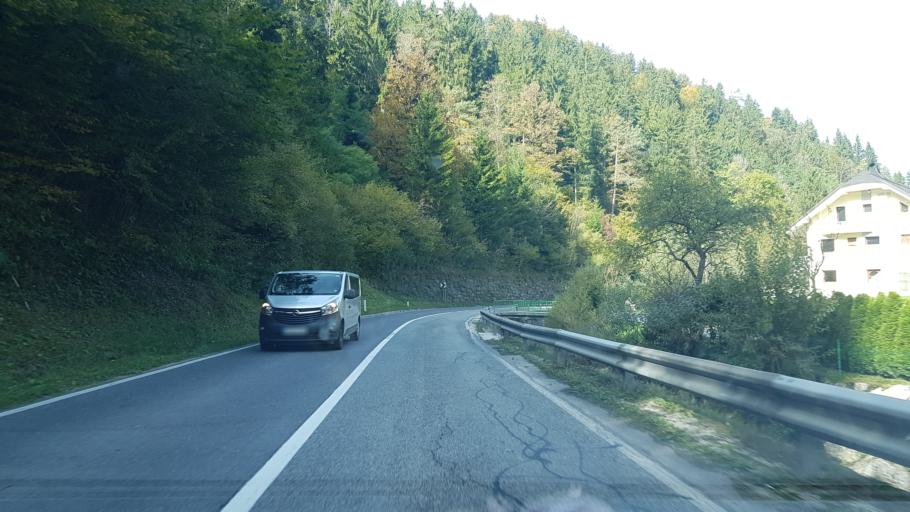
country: SI
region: Dobrna
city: Dobrna
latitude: 46.4041
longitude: 15.1794
